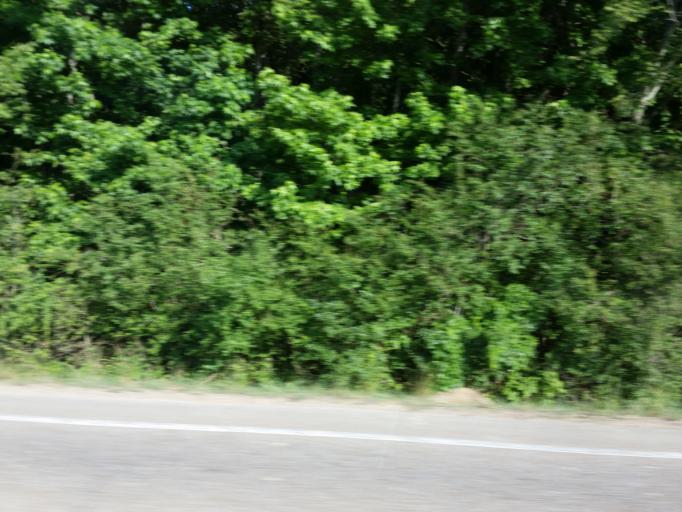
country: US
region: Mississippi
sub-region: Calhoun County
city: Calhoun City
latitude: 33.8221
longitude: -89.3405
